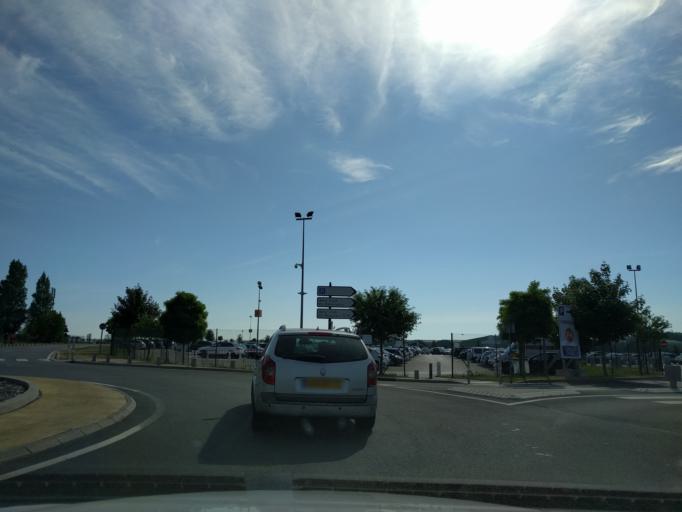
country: FR
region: Picardie
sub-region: Departement de l'Oise
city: Tille
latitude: 49.4630
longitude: 2.1180
